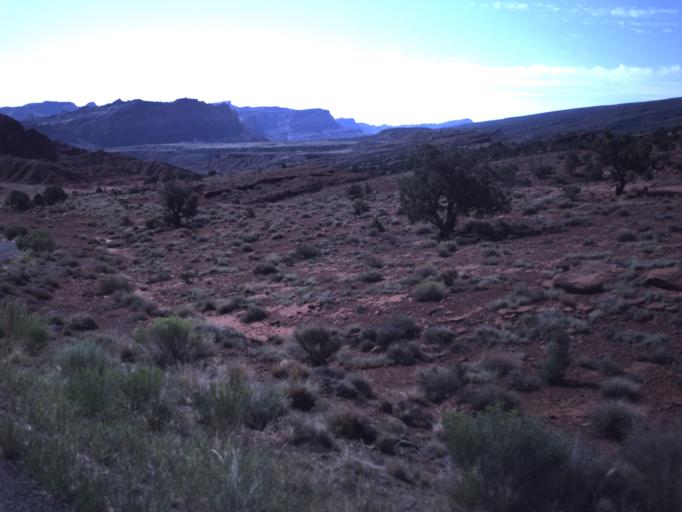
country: US
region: Utah
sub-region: Wayne County
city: Loa
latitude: 38.3076
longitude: -111.2822
